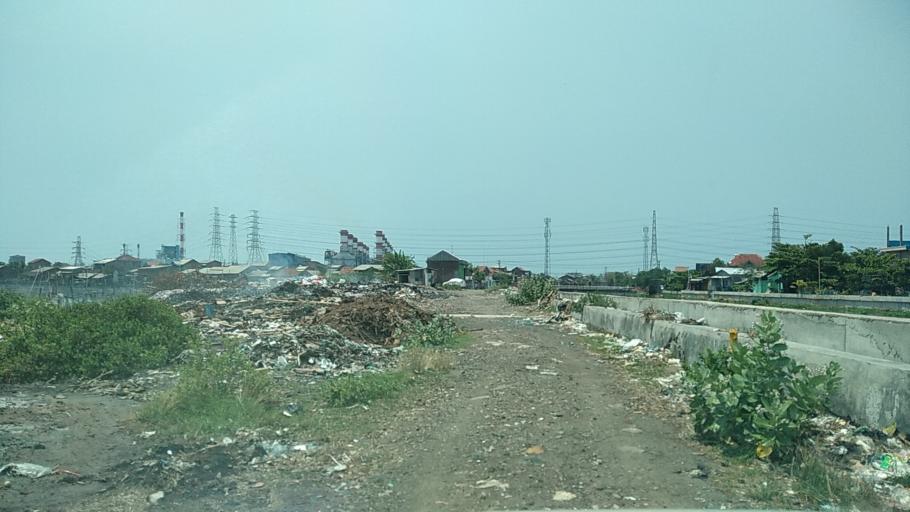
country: ID
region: Central Java
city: Semarang
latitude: -6.9556
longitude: 110.4387
